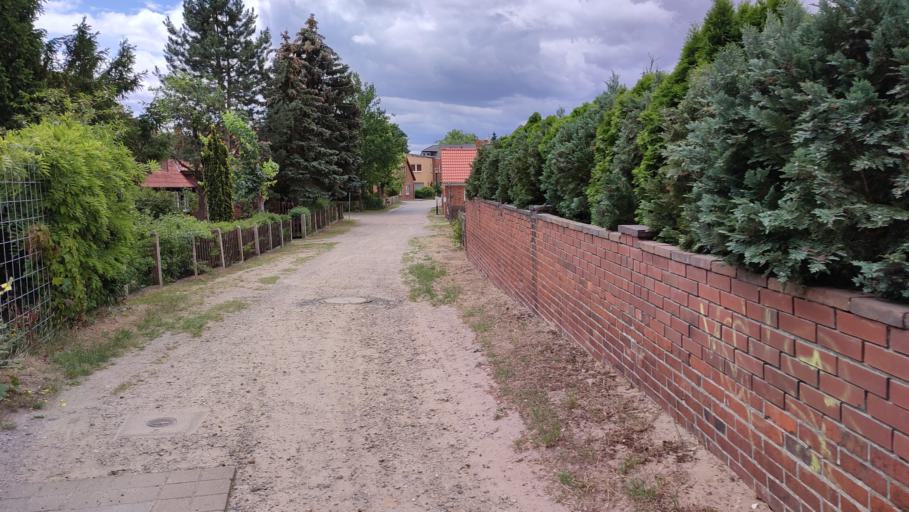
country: DE
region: Lower Saxony
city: Neu Darchau
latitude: 53.2837
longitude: 10.9329
